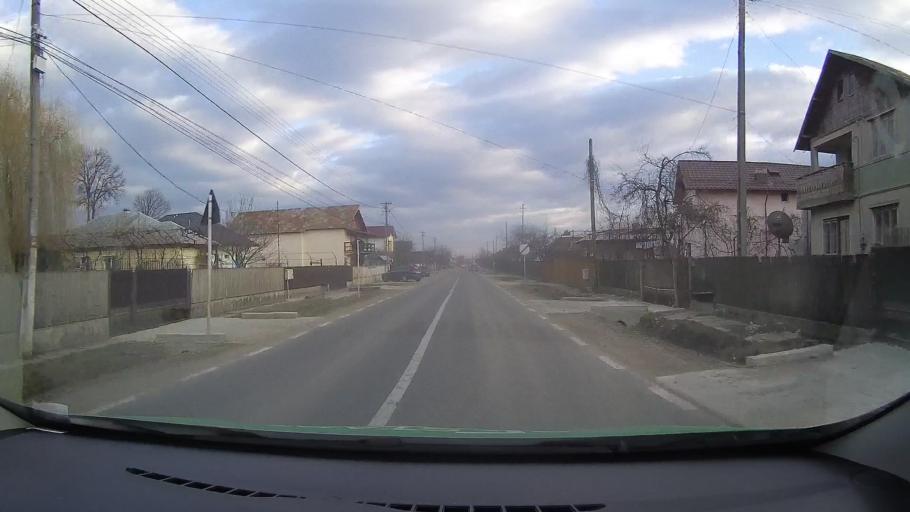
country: RO
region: Dambovita
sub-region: Comuna I. L. Caragiale
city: Ghirdoveni
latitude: 44.9312
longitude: 25.6866
